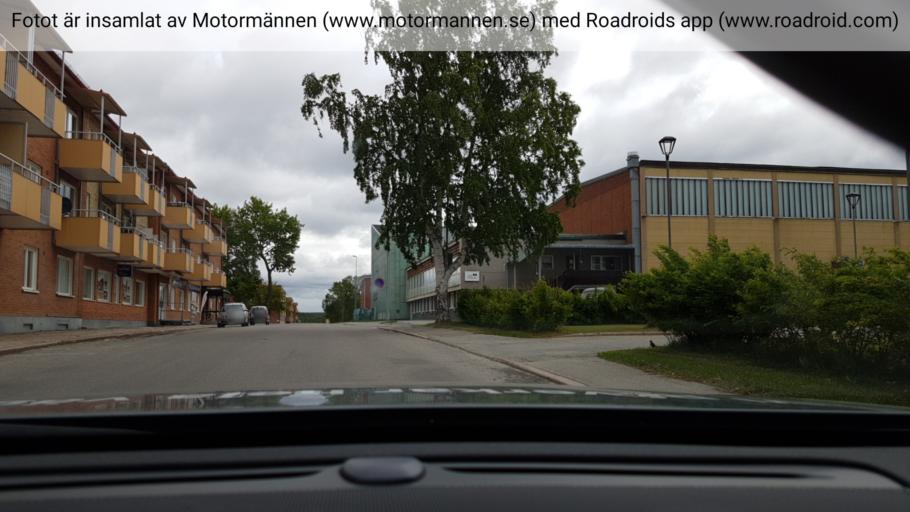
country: SE
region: Vaesterbotten
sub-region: Lycksele Kommun
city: Lycksele
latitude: 64.5957
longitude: 18.6711
